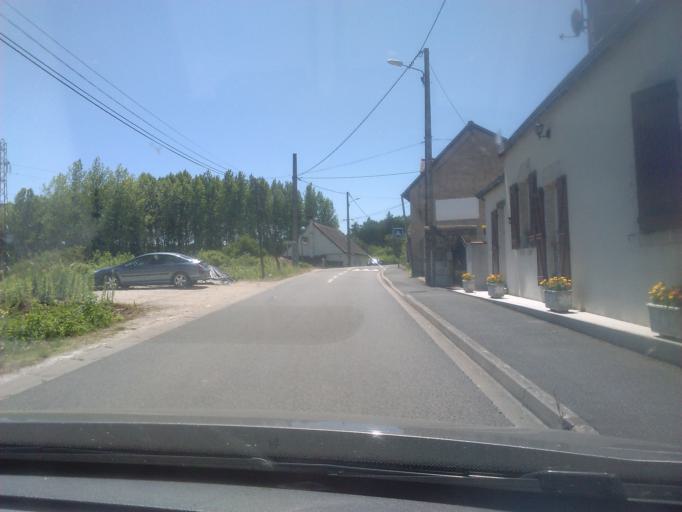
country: FR
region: Centre
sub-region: Departement du Loir-et-Cher
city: Saint-Sulpice-de-Pommeray
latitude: 47.6115
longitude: 1.2365
